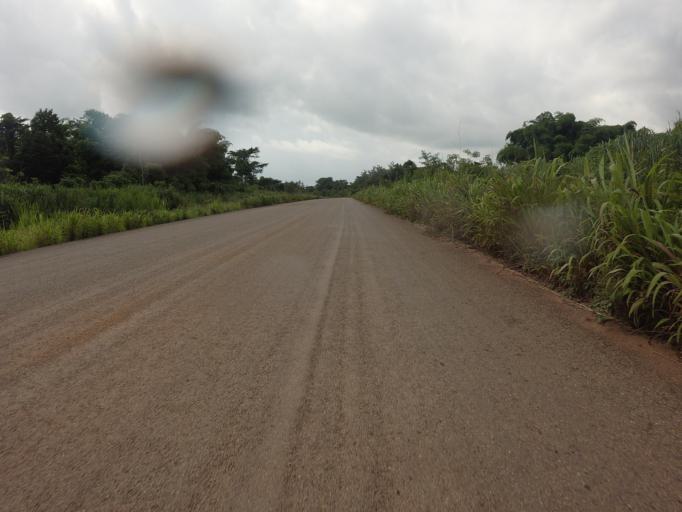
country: TG
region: Plateaux
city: Kpalime
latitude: 6.9355
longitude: 0.4632
